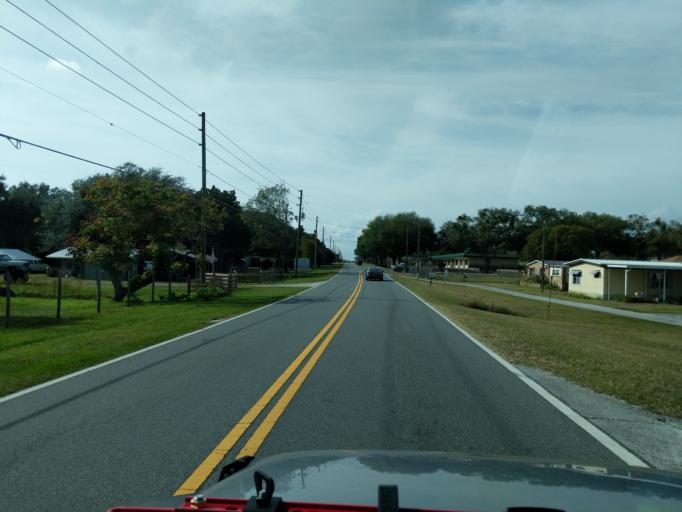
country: US
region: Florida
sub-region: Lake County
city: Tavares
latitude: 28.8039
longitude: -81.7090
